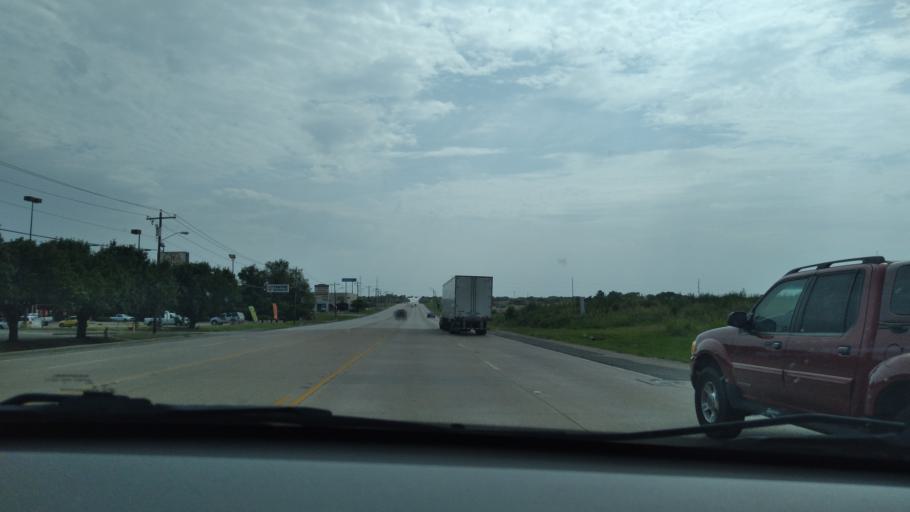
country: US
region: Texas
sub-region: Navarro County
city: Corsicana
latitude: 32.0701
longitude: -96.5052
